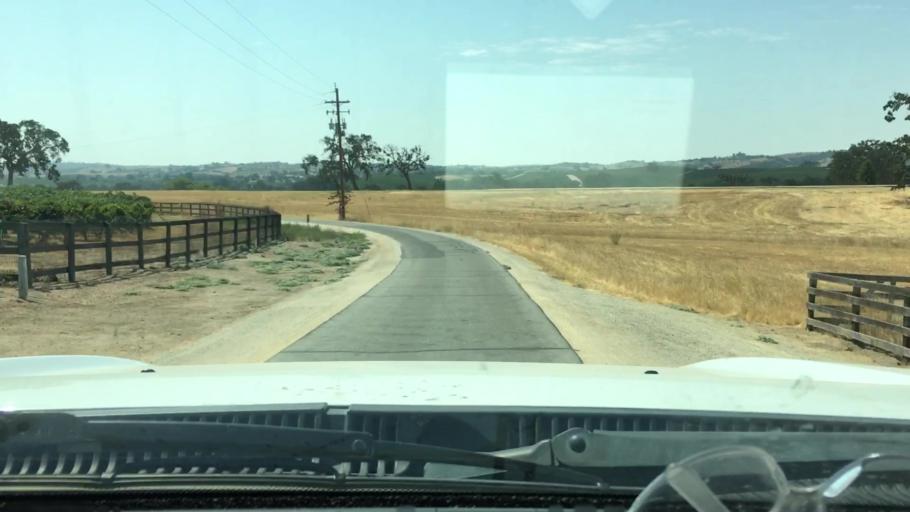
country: US
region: California
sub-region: San Luis Obispo County
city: Paso Robles
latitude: 35.5760
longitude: -120.6030
